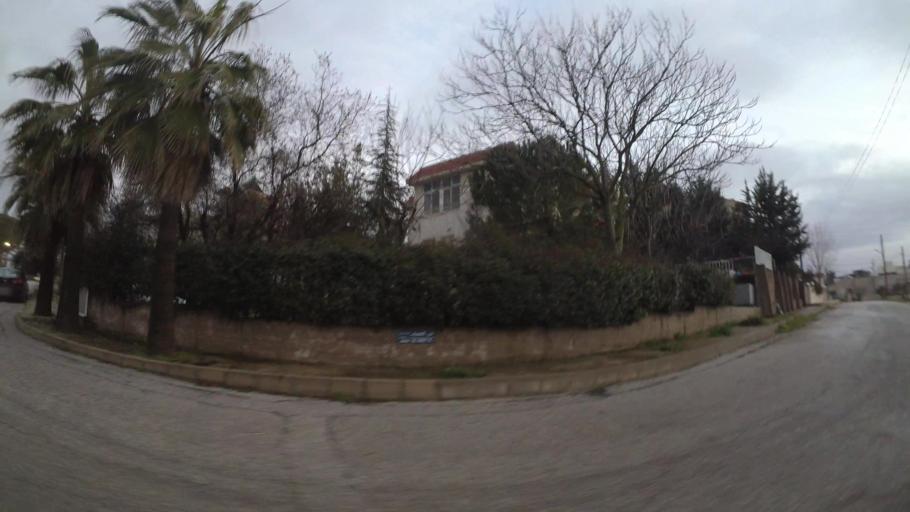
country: JO
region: Amman
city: Al Jubayhah
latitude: 32.0306
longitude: 35.8087
